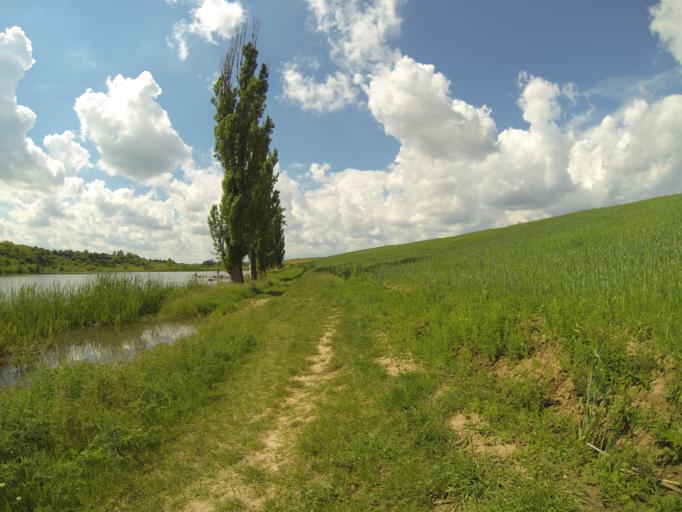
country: RO
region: Dolj
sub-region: Comuna Malu Mare
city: Preajba
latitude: 44.2668
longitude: 23.8541
